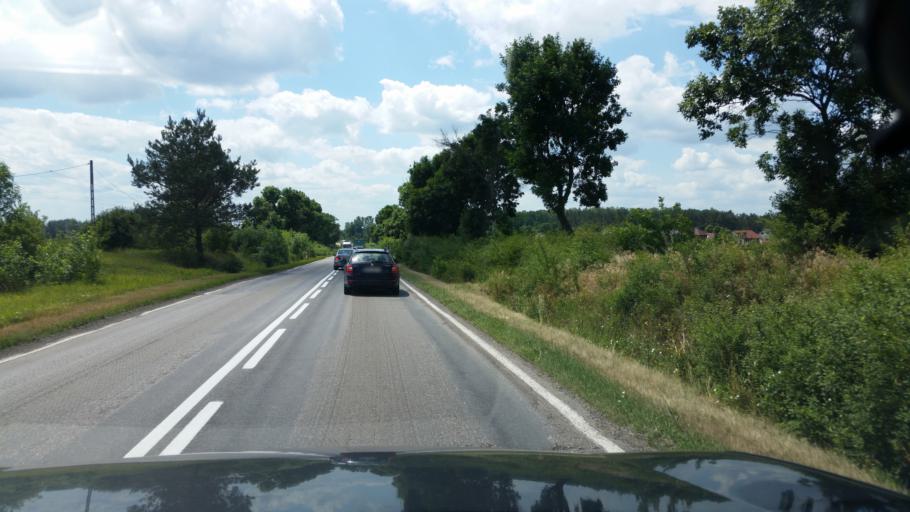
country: PL
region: Podlasie
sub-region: Powiat lomzynski
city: Sniadowo
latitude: 53.0647
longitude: 22.0056
